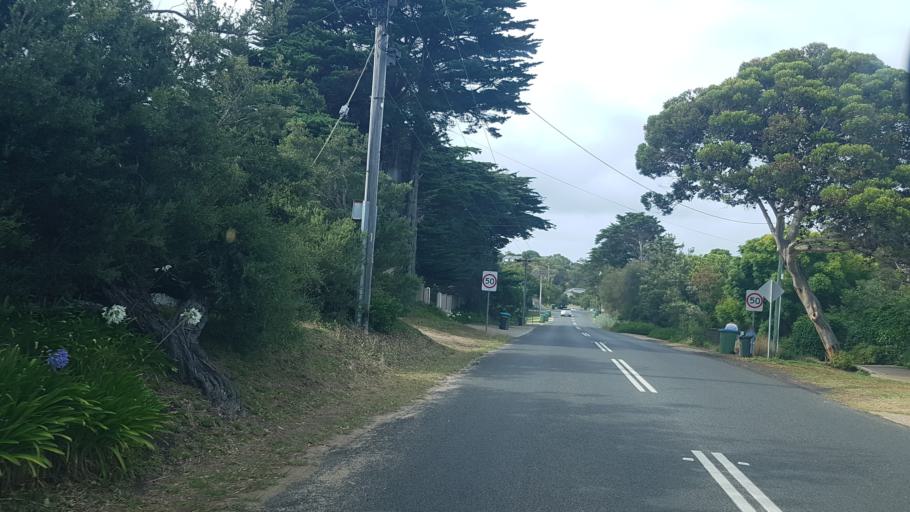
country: AU
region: Victoria
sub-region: Mornington Peninsula
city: Sorrento
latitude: -38.3240
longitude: 144.7112
